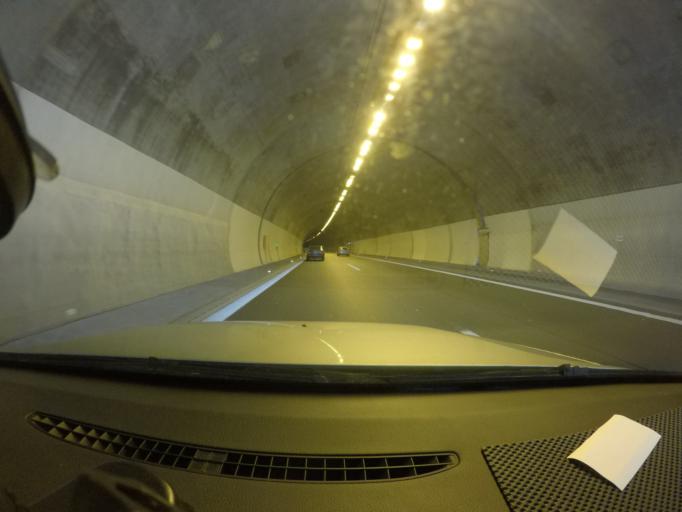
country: DE
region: Baden-Wuerttemberg
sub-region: Regierungsbezirk Stuttgart
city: Nufringen
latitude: 48.6072
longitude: 8.8970
